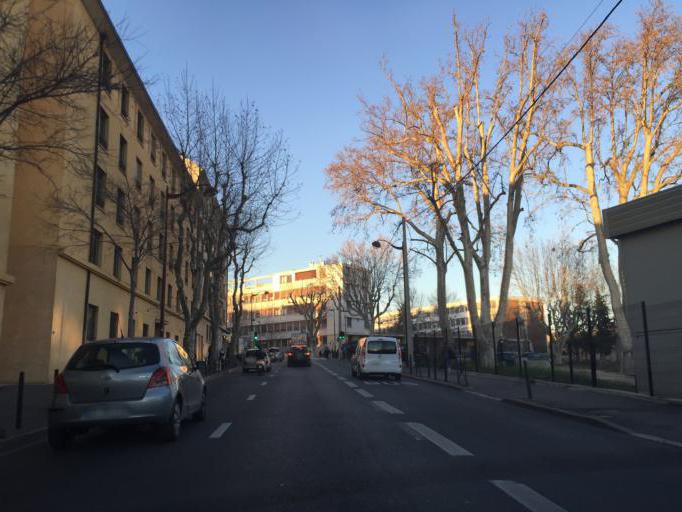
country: FR
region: Provence-Alpes-Cote d'Azur
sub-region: Departement des Bouches-du-Rhone
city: Aix-en-Provence
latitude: 43.5266
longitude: 5.4550
